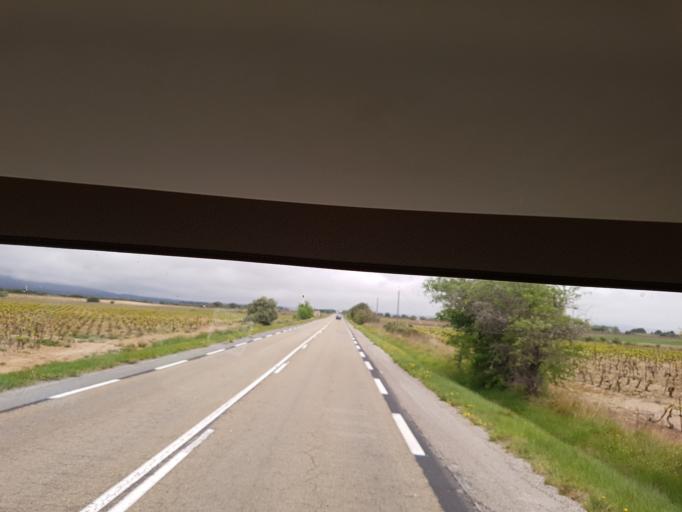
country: FR
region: Languedoc-Roussillon
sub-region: Departement de l'Aude
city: Leucate
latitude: 42.9193
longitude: 2.9963
